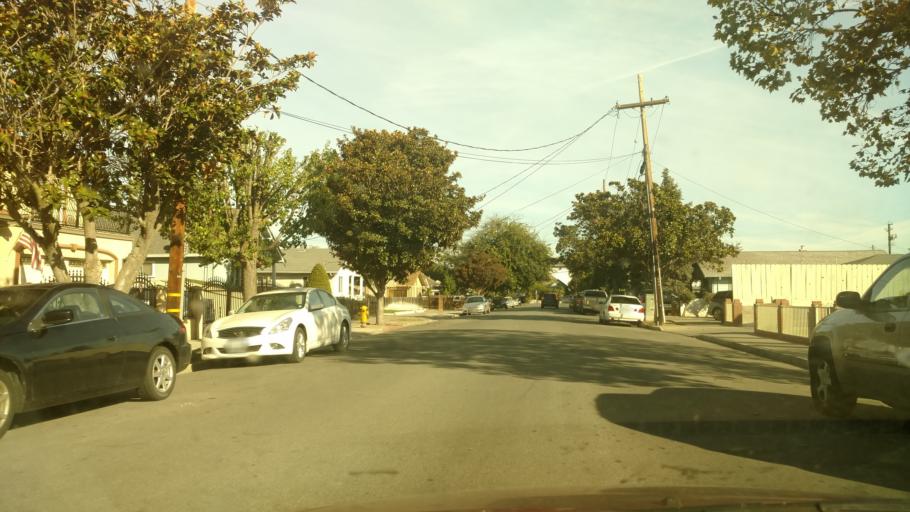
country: US
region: California
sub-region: San Benito County
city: Hollister
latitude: 36.8451
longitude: -121.3990
